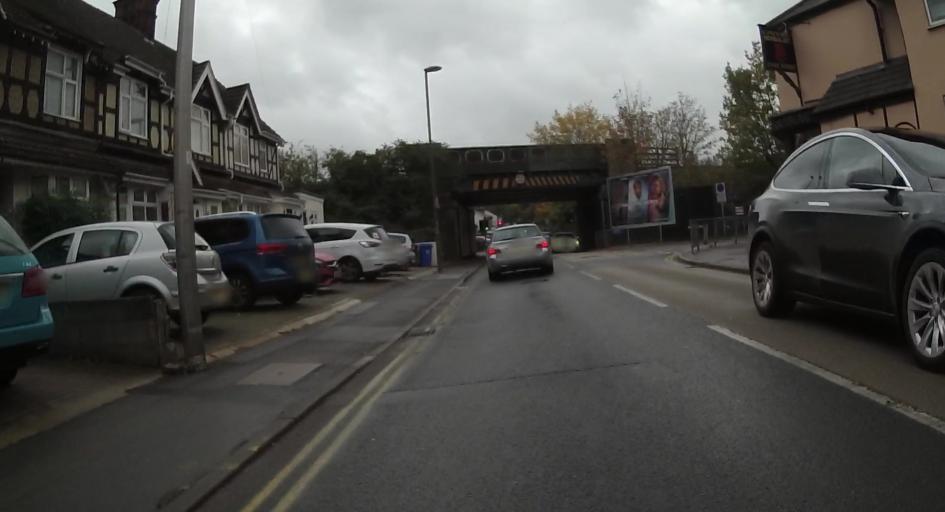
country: GB
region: England
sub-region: Surrey
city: Woking
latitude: 51.3251
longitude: -0.5421
